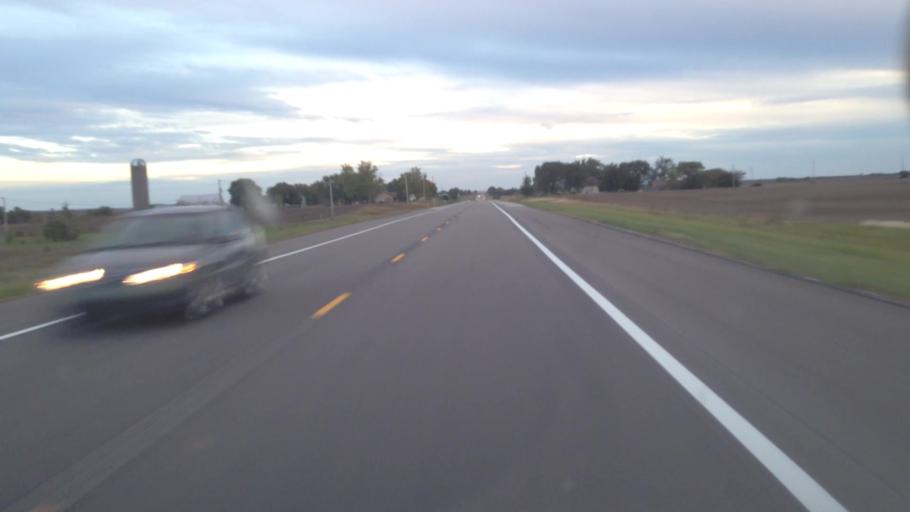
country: US
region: Kansas
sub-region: Anderson County
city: Garnett
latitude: 38.3877
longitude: -95.2488
